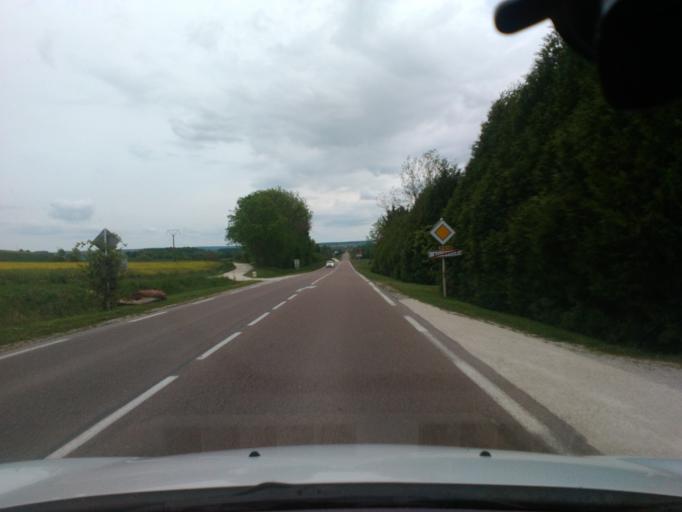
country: FR
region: Champagne-Ardenne
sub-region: Departement de l'Aube
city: Bar-sur-Aube
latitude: 48.2522
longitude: 4.6851
